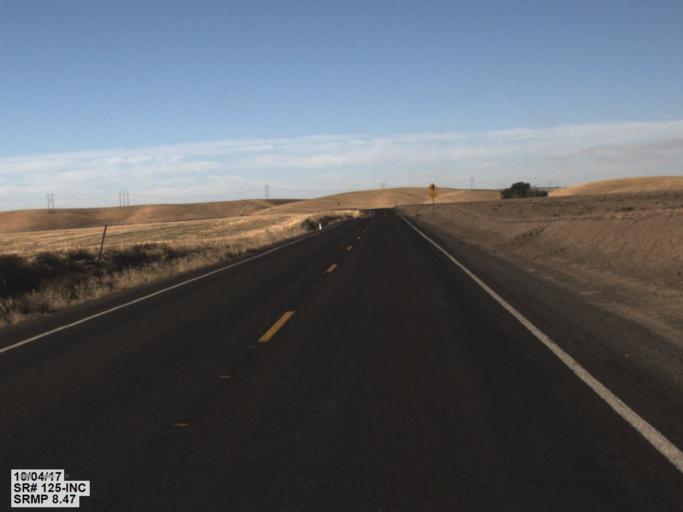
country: US
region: Washington
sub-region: Walla Walla County
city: Walla Walla
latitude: 46.0967
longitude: -118.3694
